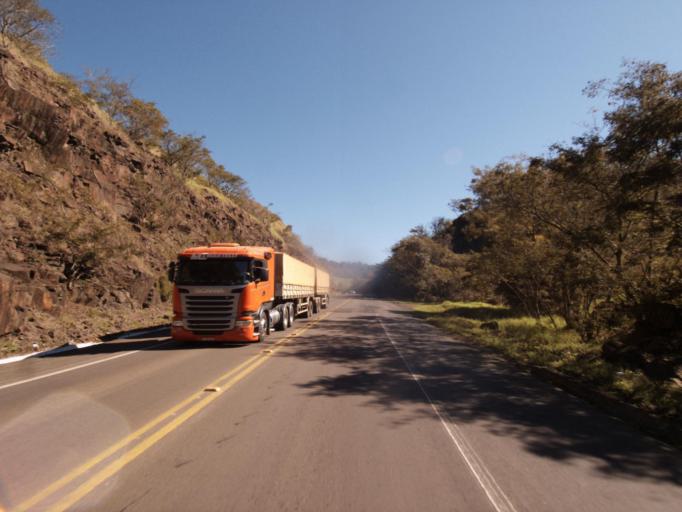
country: BR
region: Rio Grande do Sul
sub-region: Frederico Westphalen
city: Frederico Westphalen
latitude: -26.8261
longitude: -53.4147
